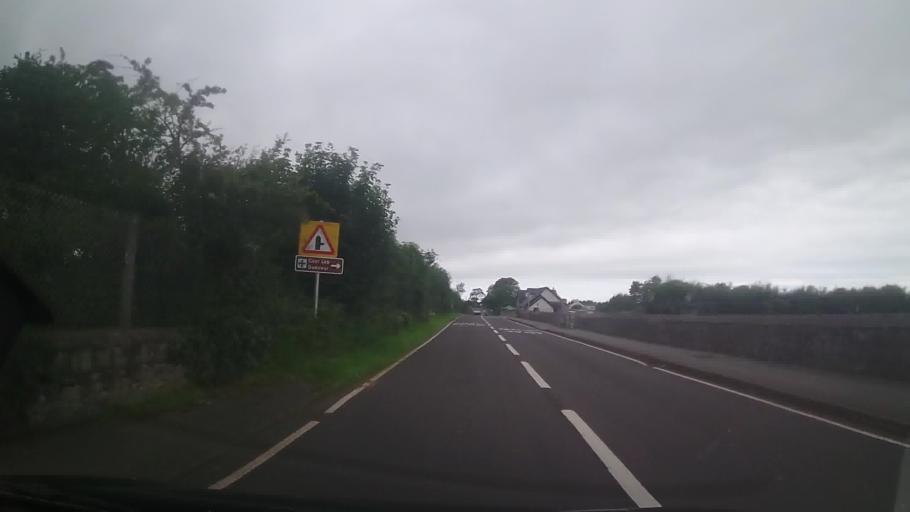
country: GB
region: Wales
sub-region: Gwynedd
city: Caernarfon
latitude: 53.1808
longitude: -4.2783
